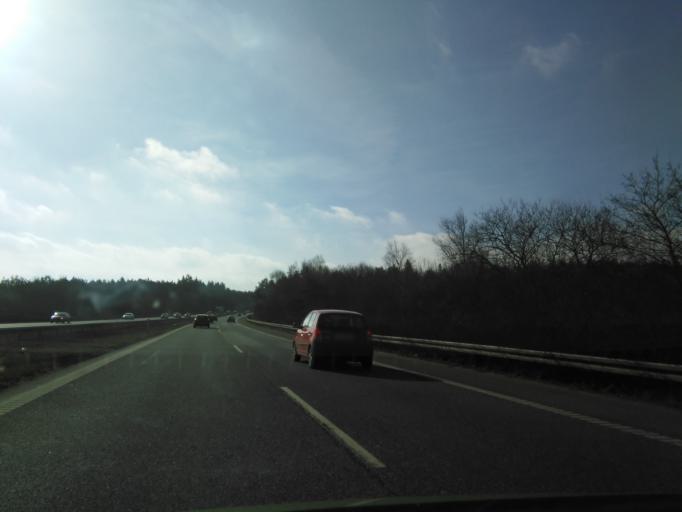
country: DK
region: Central Jutland
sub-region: Skanderborg Kommune
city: Skanderborg
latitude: 56.0151
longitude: 9.8825
